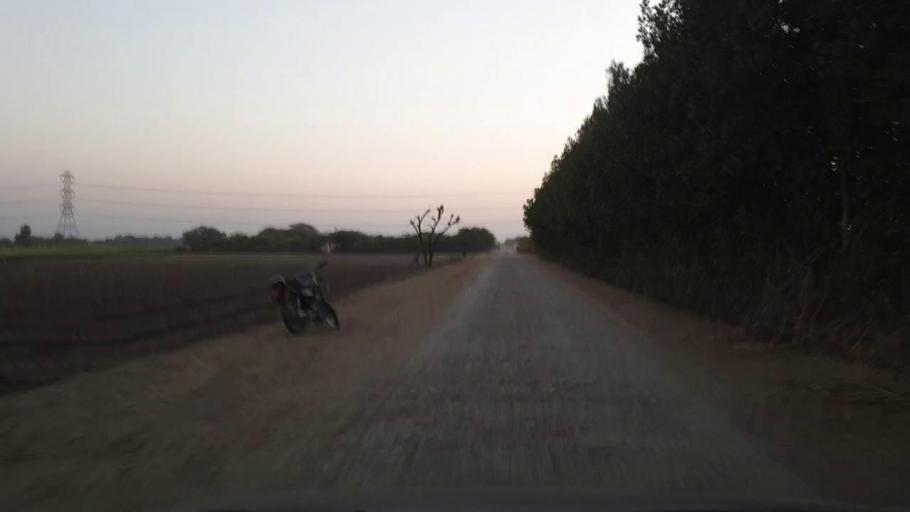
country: PK
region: Sindh
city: Digri
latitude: 25.1990
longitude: 69.1935
